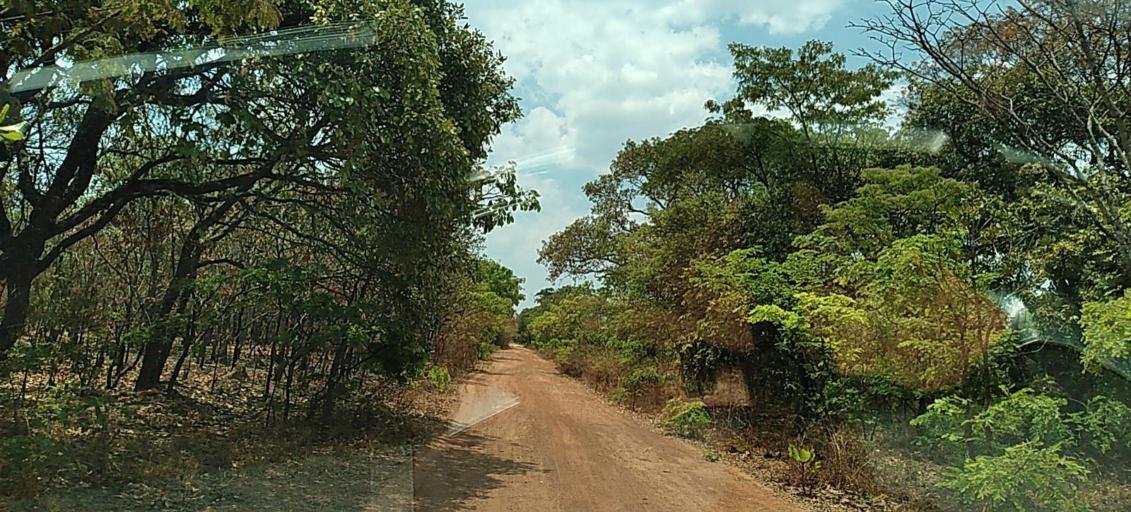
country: ZM
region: Copperbelt
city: Chililabombwe
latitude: -12.5300
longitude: 27.6289
